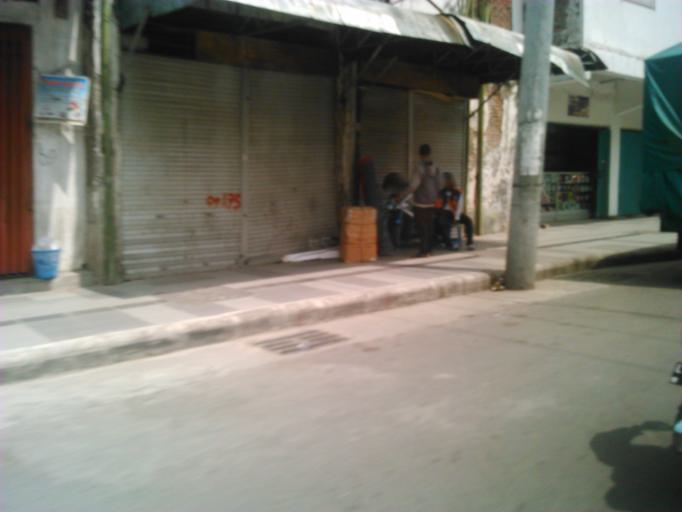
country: ID
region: East Java
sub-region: Kota Surabaya
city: Surabaya
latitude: -7.2469
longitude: 112.7352
